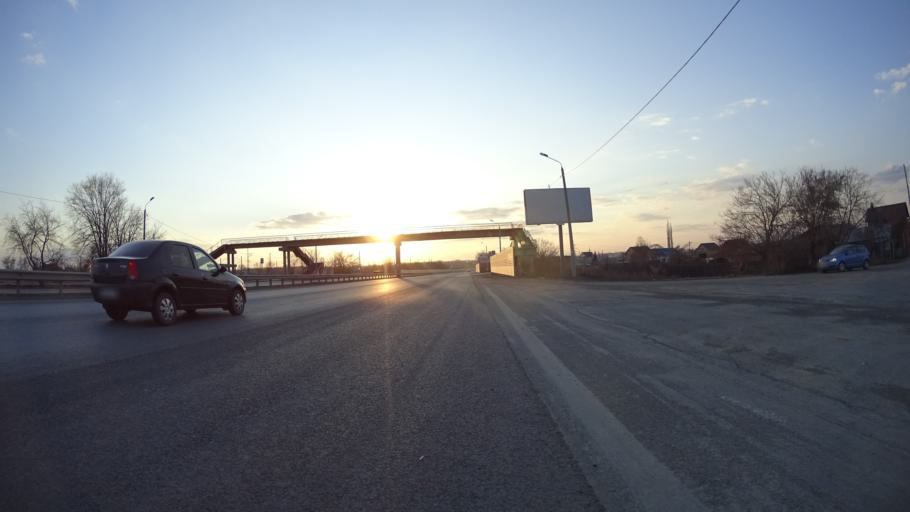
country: RU
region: Chelyabinsk
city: Novosineglazovskiy
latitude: 55.0422
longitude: 61.4303
